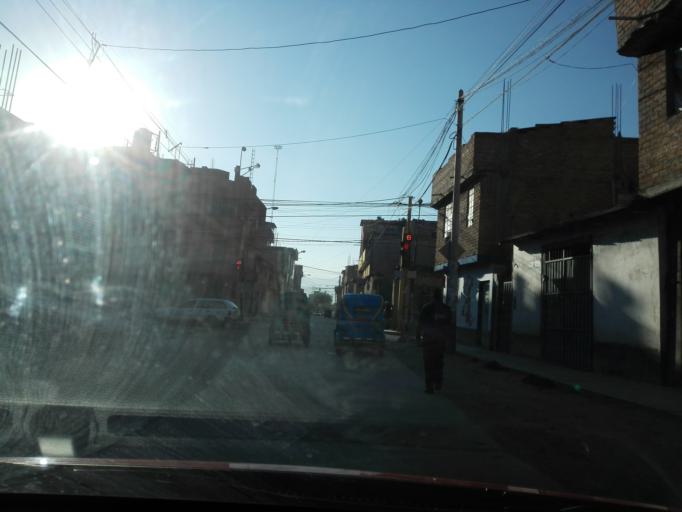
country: PE
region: Ayacucho
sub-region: Provincia de Huamanga
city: Ayacucho
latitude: -13.1566
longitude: -74.2221
